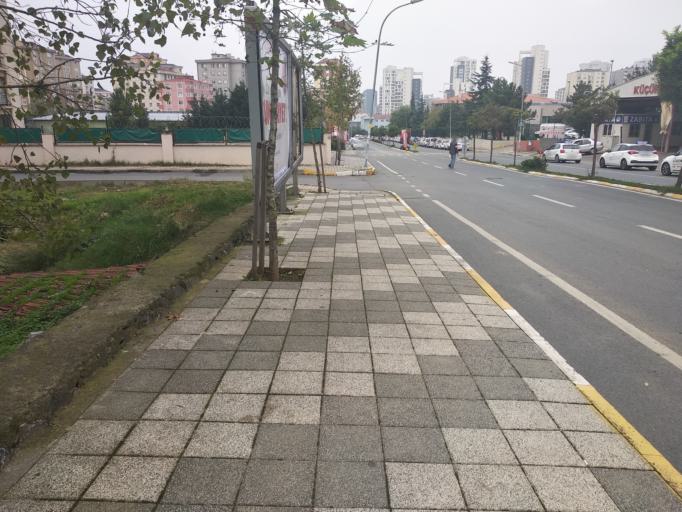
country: TR
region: Istanbul
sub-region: Atasehir
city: Atasehir
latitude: 40.9827
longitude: 29.1267
